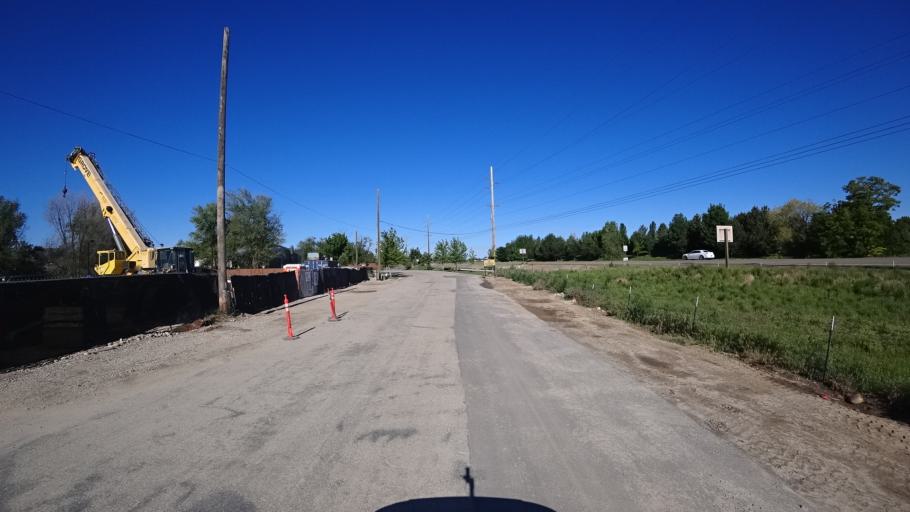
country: US
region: Idaho
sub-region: Ada County
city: Eagle
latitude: 43.6934
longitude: -116.4156
